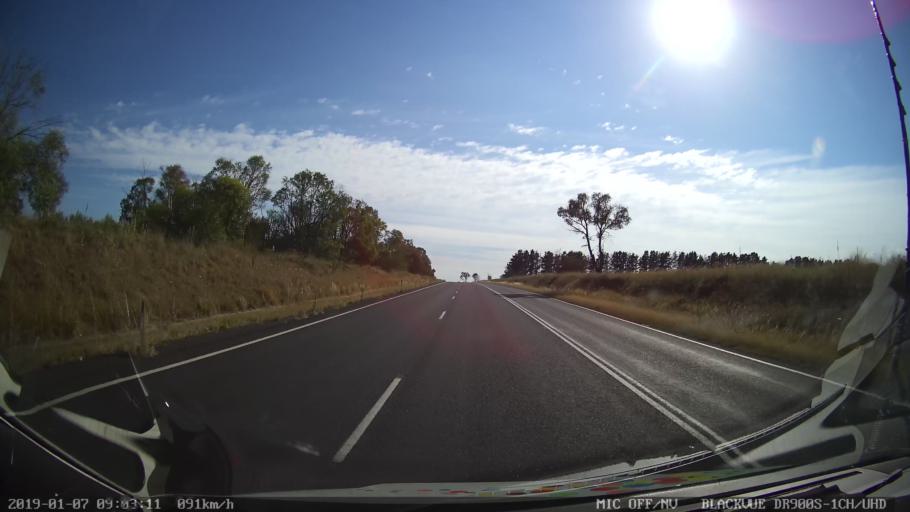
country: AU
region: New South Wales
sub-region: Armidale Dumaresq
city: Armidale
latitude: -30.7304
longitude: 151.4344
